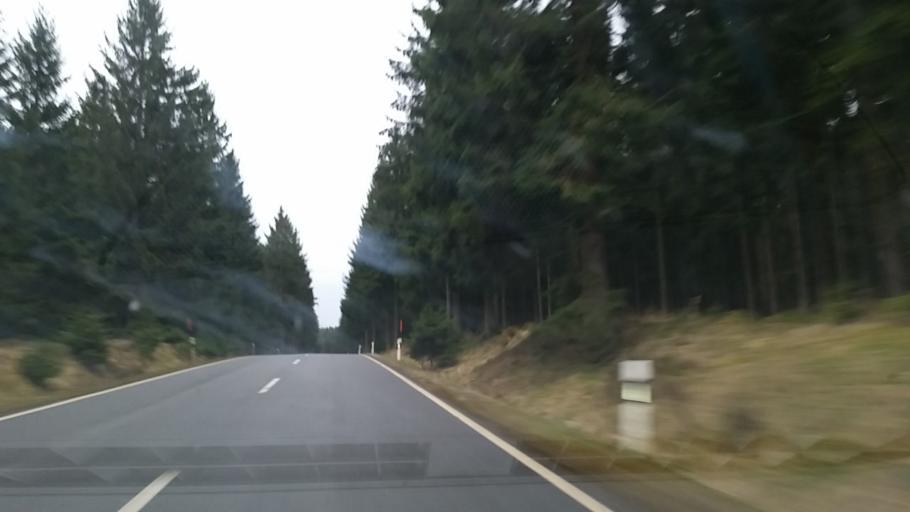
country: DE
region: Saxony-Anhalt
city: Benneckenstein
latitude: 51.6514
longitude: 10.6867
